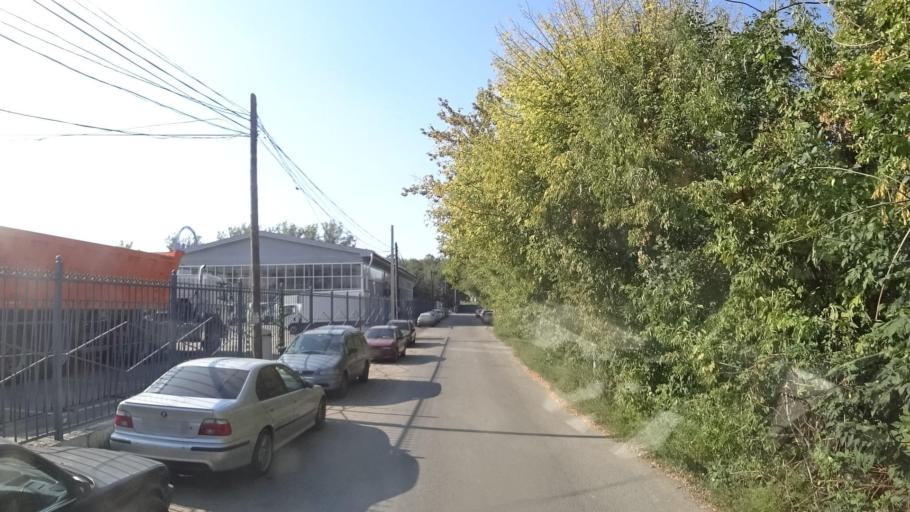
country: KZ
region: Almaty Qalasy
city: Almaty
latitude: 43.2883
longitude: 76.9231
